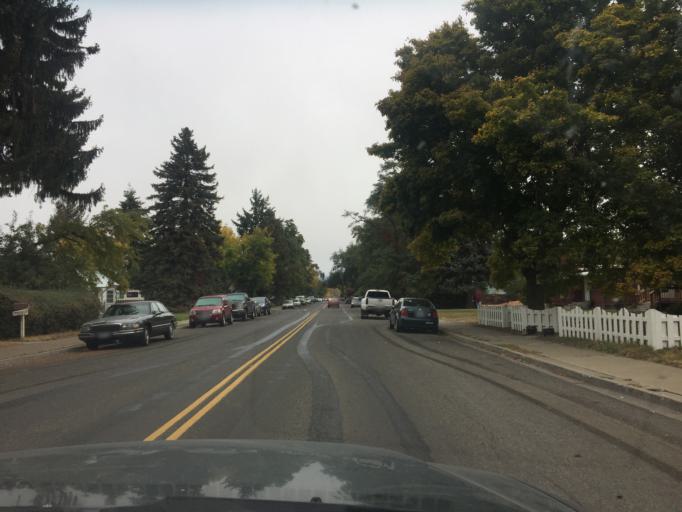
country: US
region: Washington
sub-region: Kittitas County
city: Ellensburg
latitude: 46.9886
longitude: -120.5455
